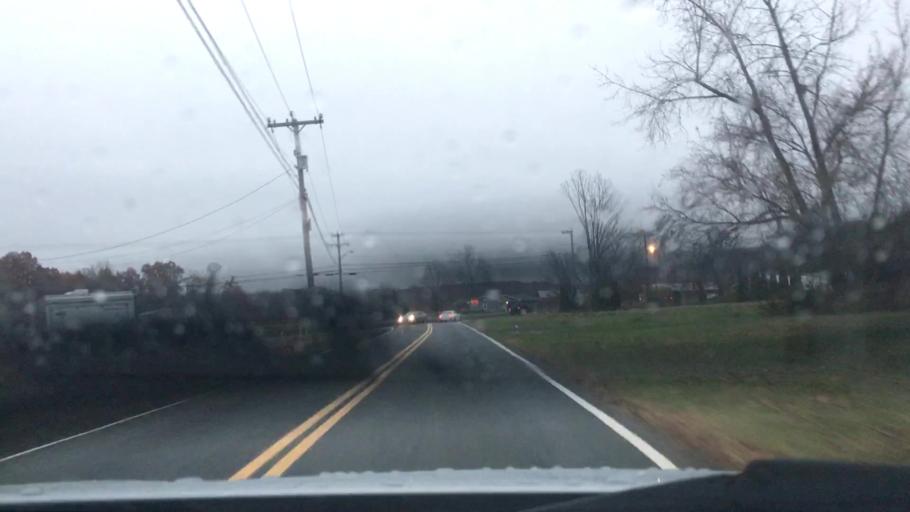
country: US
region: Massachusetts
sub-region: Hampden County
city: Southwick
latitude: 42.0787
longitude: -72.7692
